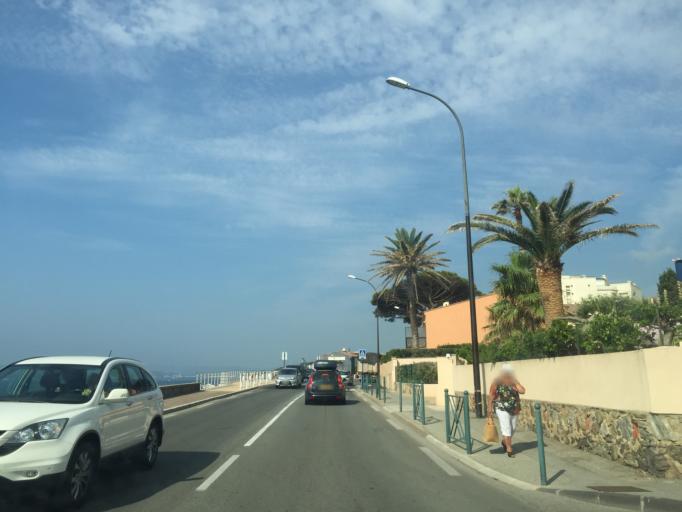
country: FR
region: Provence-Alpes-Cote d'Azur
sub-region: Departement du Var
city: Sainte-Maxime
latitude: 43.3068
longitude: 6.6458
